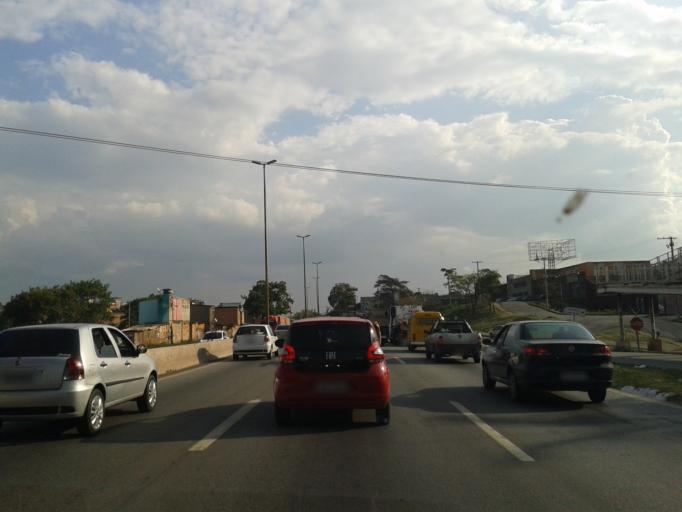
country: BR
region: Minas Gerais
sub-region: Belo Horizonte
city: Belo Horizonte
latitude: -19.8718
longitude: -43.9483
